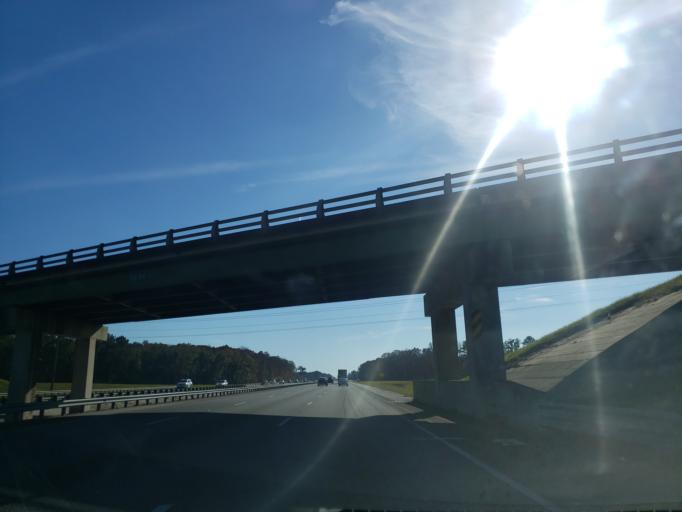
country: US
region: Georgia
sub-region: McIntosh County
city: Darien
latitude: 31.5321
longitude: -81.4459
